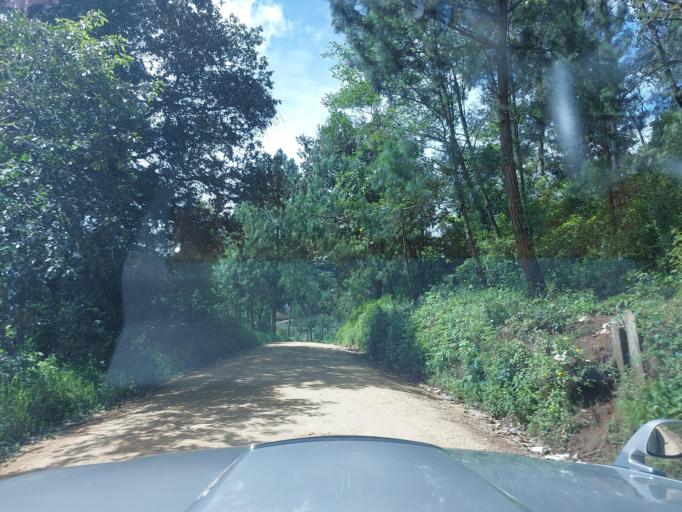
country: GT
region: Chimaltenango
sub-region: Municipio de San Juan Comalapa
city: Comalapa
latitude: 14.7534
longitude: -90.8711
